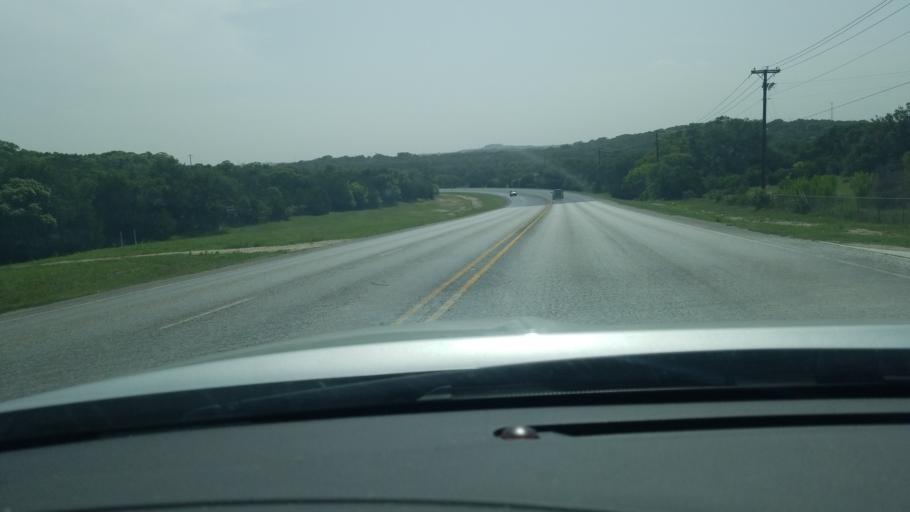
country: US
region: Texas
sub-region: Comal County
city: Bulverde
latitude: 29.7969
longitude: -98.4574
